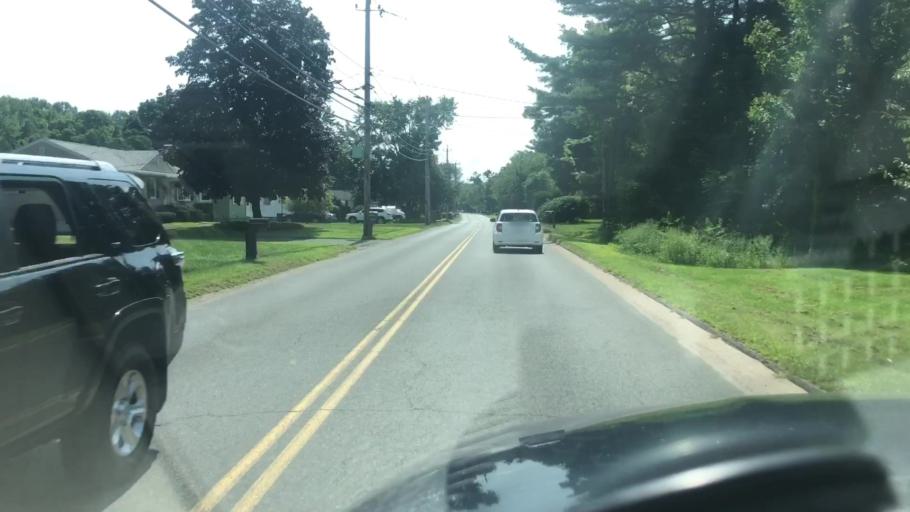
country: US
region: Massachusetts
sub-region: Hampden County
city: Westfield
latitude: 42.1443
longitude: -72.6999
